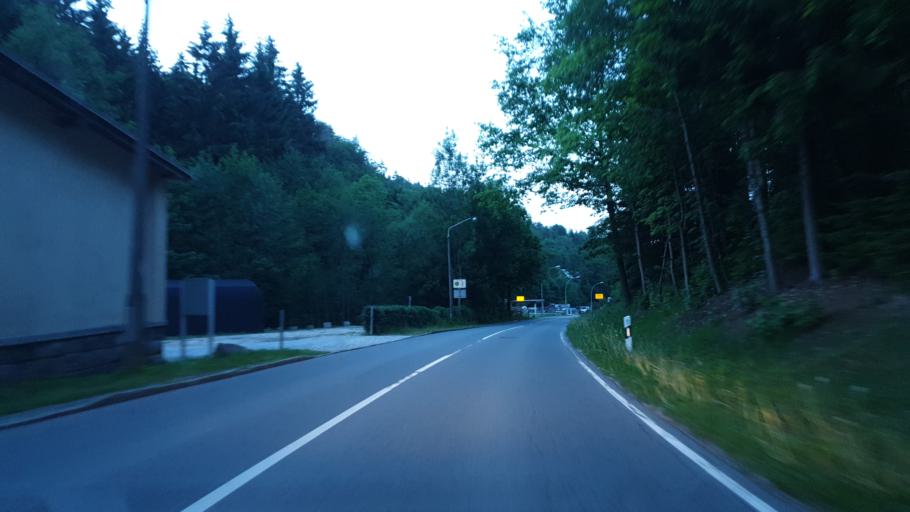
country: DE
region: Saxony
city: Zschorlau
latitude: 50.5827
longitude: 12.6585
